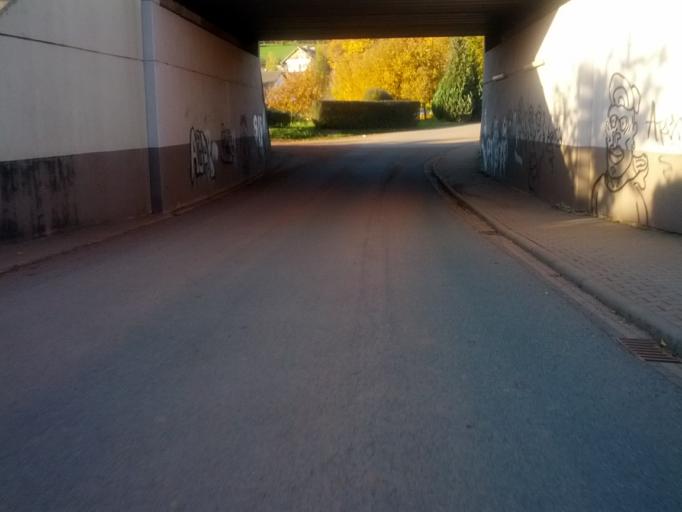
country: DE
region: Thuringia
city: Seebach
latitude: 50.9431
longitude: 10.4598
